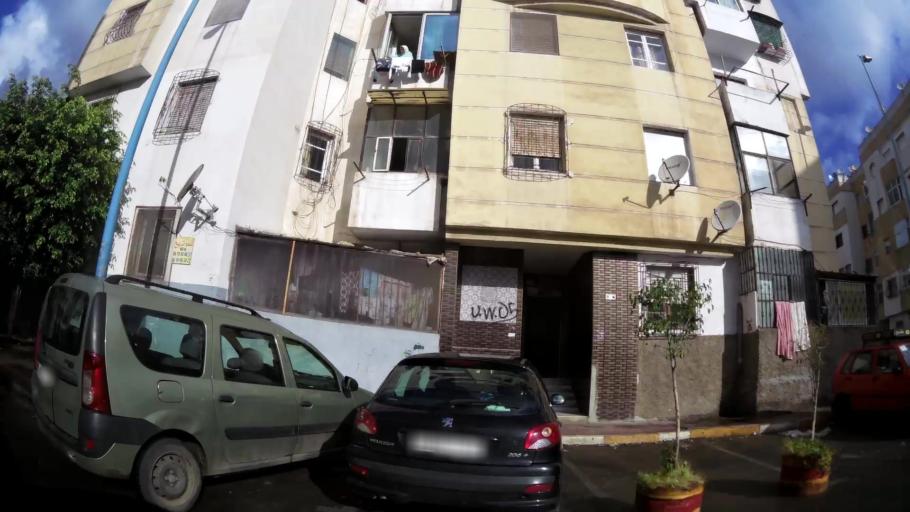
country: MA
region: Grand Casablanca
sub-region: Mediouna
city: Tit Mellil
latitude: 33.5997
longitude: -7.5341
